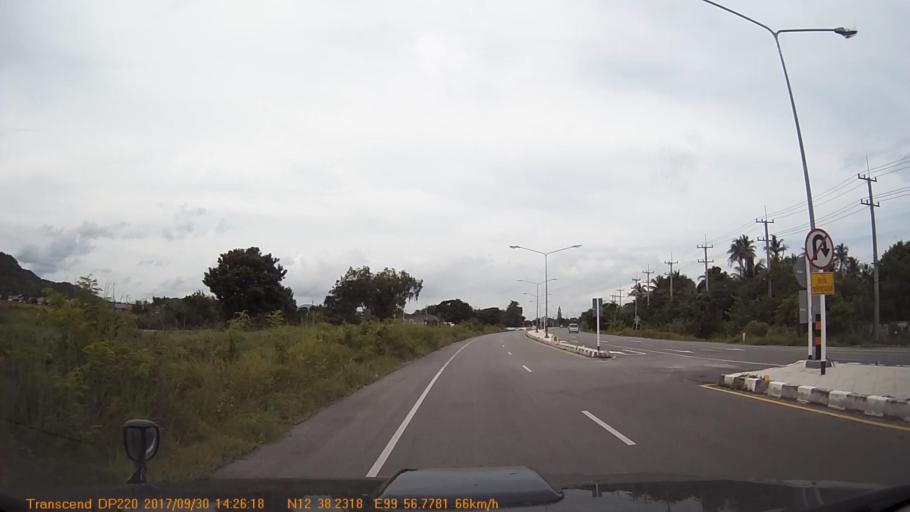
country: TH
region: Prachuap Khiri Khan
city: Hua Hin
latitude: 12.6379
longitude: 99.9462
